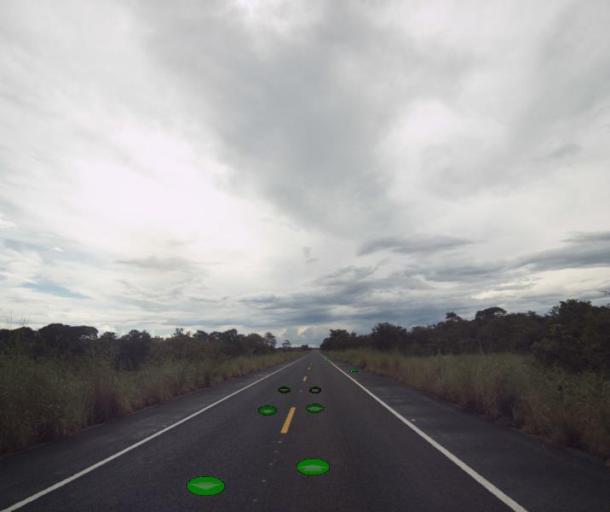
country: BR
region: Goias
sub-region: Sao Miguel Do Araguaia
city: Sao Miguel do Araguaia
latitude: -13.2505
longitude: -50.5294
